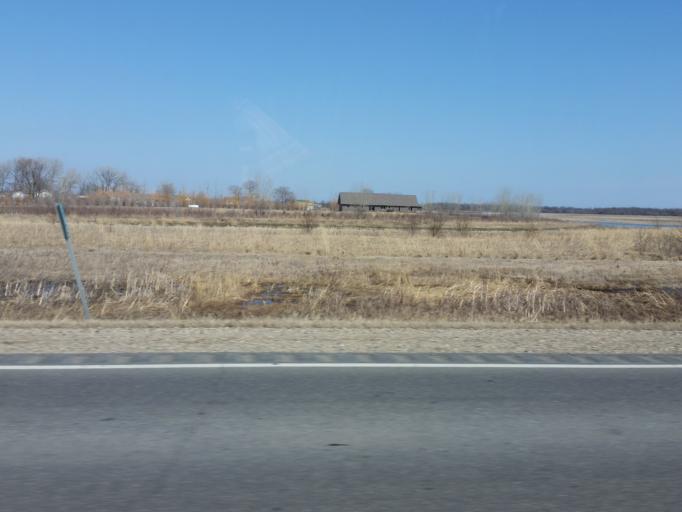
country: US
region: North Dakota
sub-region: Grand Forks County
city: Grand Forks Air Force Base
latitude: 48.0954
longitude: -97.1974
